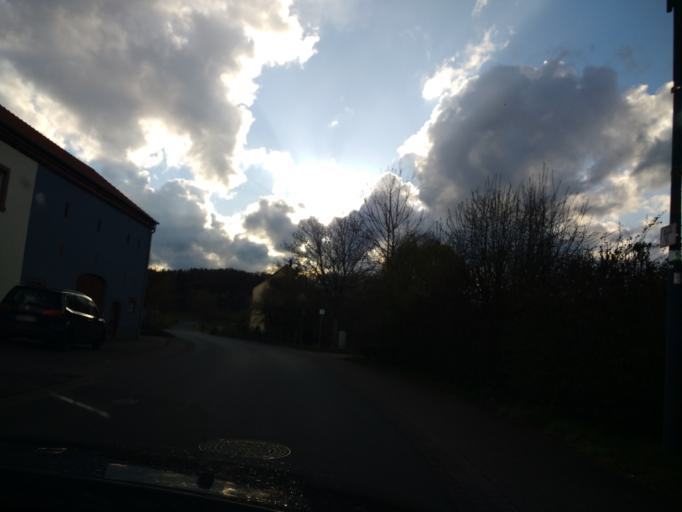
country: DE
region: Rheinland-Pfalz
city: Oberbettingen
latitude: 50.2860
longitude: 6.6218
